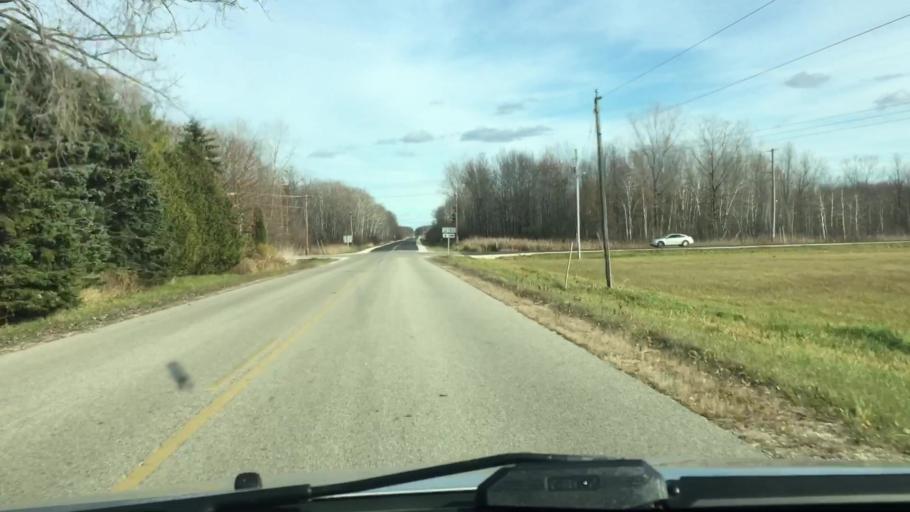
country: US
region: Wisconsin
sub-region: Kewaunee County
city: Algoma
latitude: 44.6903
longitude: -87.5606
